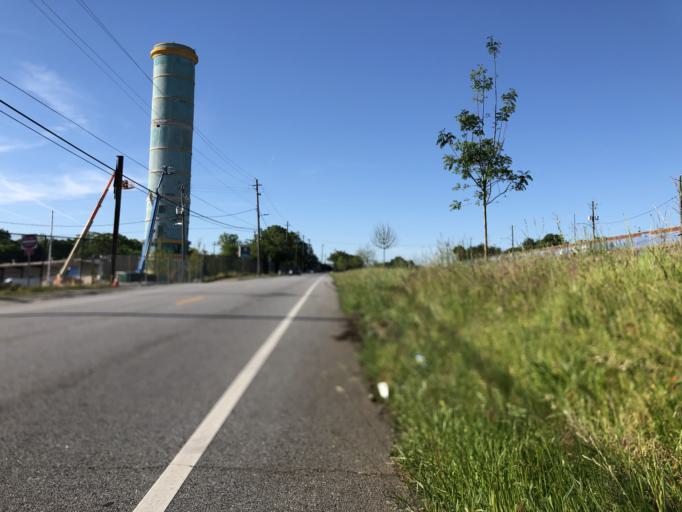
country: US
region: Georgia
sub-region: Fulton County
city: Atlanta
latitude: 33.7365
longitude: -84.4125
